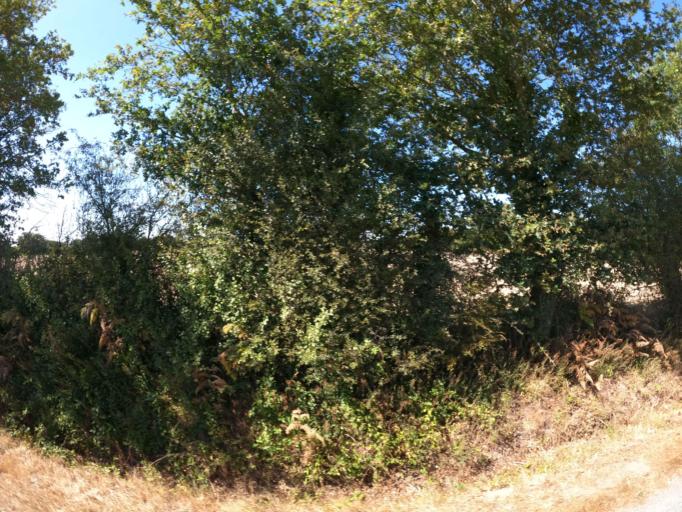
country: FR
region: Pays de la Loire
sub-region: Departement de la Vendee
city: La Gaubretiere
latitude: 46.9699
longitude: -1.0682
